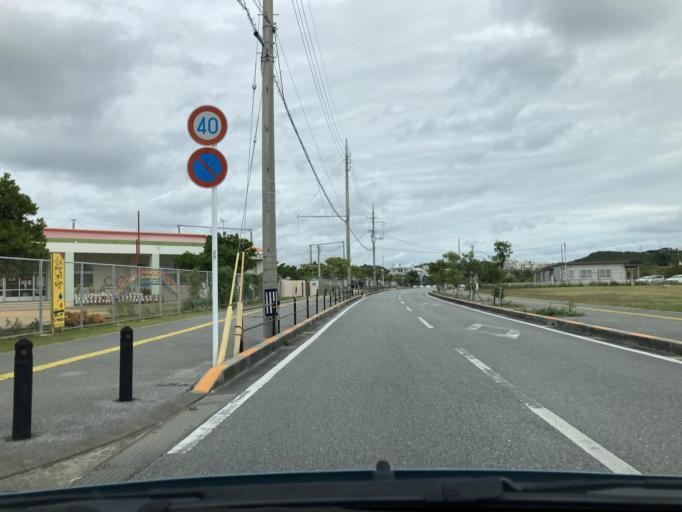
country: JP
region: Okinawa
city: Itoman
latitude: 26.1567
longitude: 127.6635
